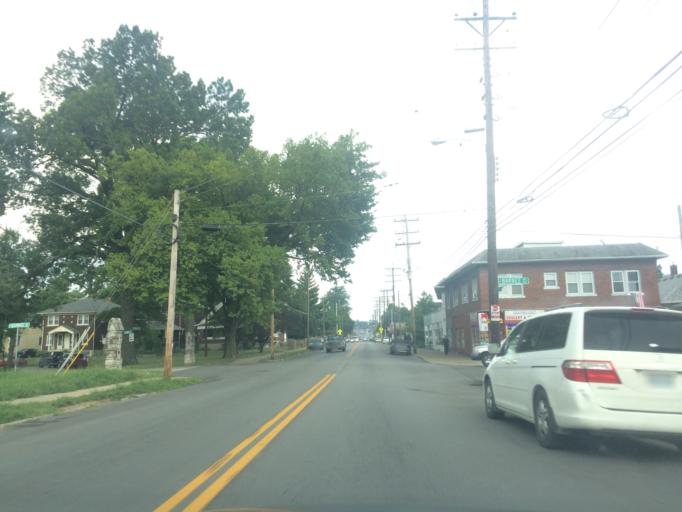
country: US
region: Kentucky
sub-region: Jefferson County
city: Audubon Park
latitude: 38.2191
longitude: -85.7474
